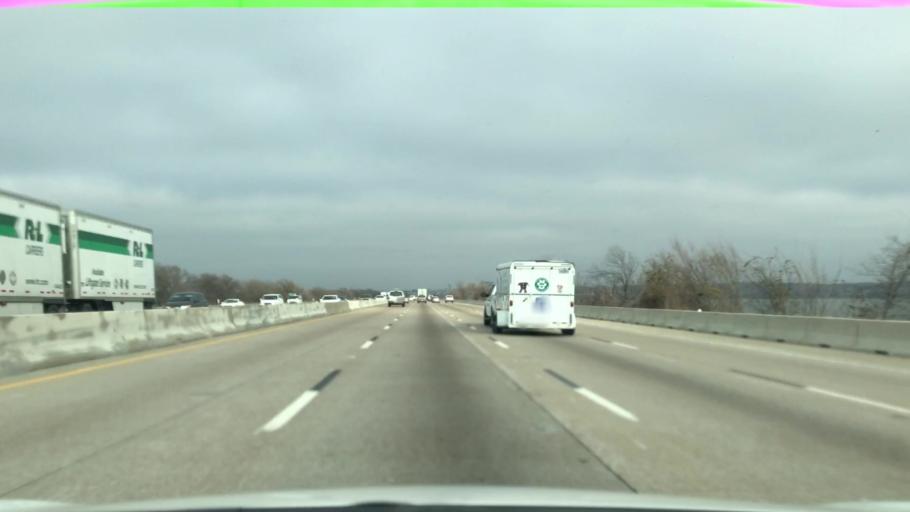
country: US
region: Texas
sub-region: Rockwall County
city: Heath
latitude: 32.8817
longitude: -96.5070
